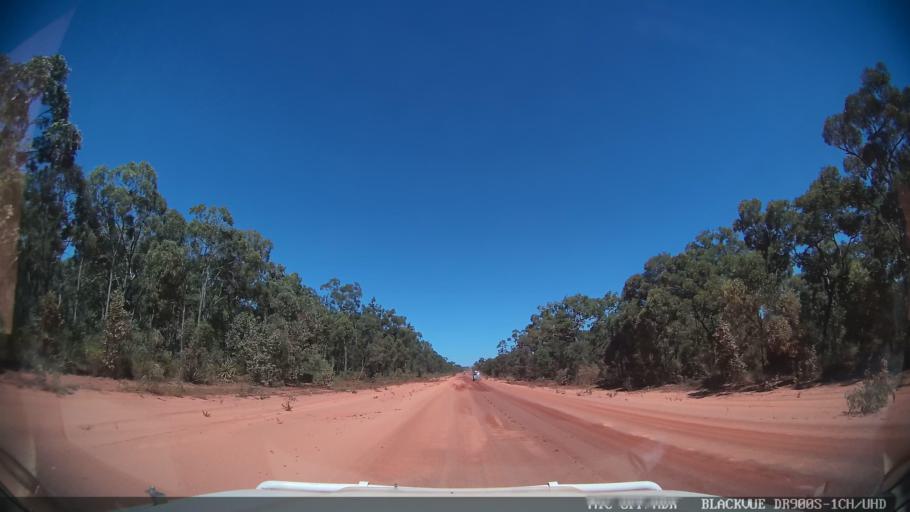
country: AU
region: Queensland
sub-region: Torres
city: Thursday Island
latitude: -11.3696
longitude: 142.3483
